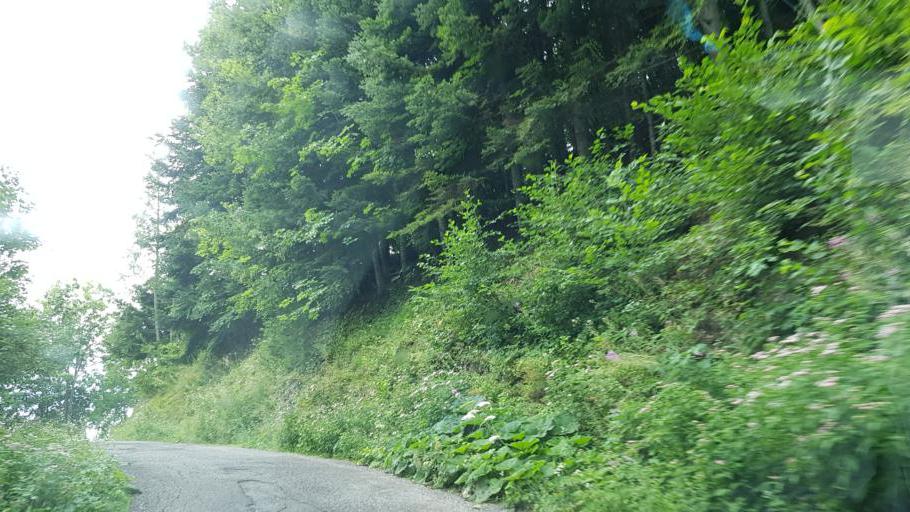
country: IT
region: Piedmont
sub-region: Provincia di Cuneo
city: Stroppo
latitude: 44.5120
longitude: 7.1126
